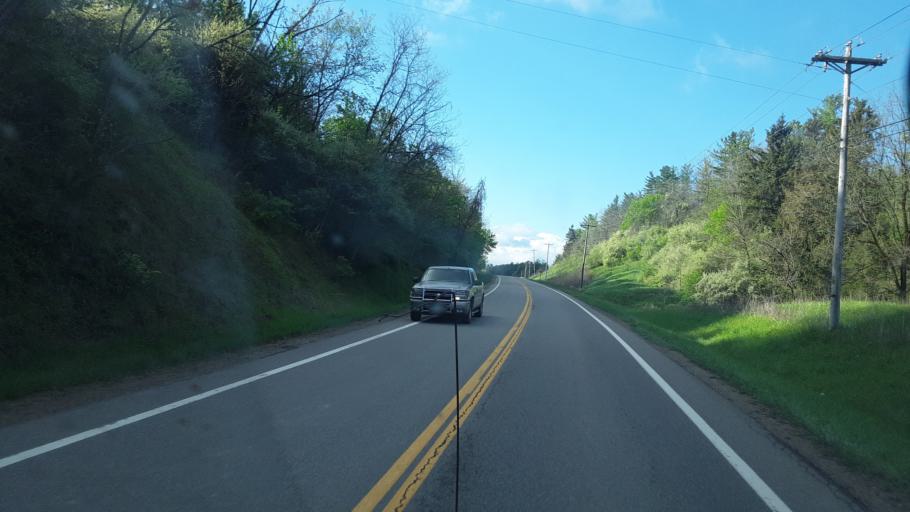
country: US
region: Ohio
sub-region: Muskingum County
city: New Concord
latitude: 39.8792
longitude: -81.6746
